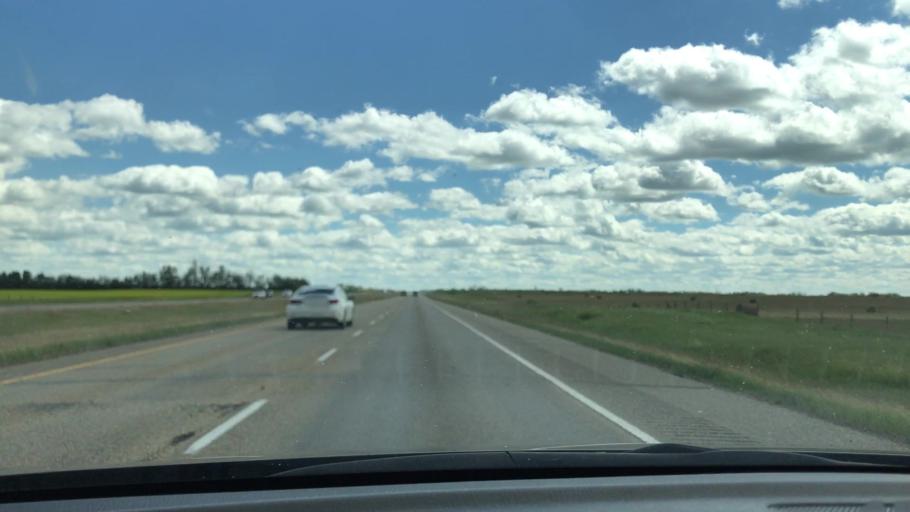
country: CA
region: Alberta
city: Leduc
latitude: 53.1606
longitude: -113.5985
